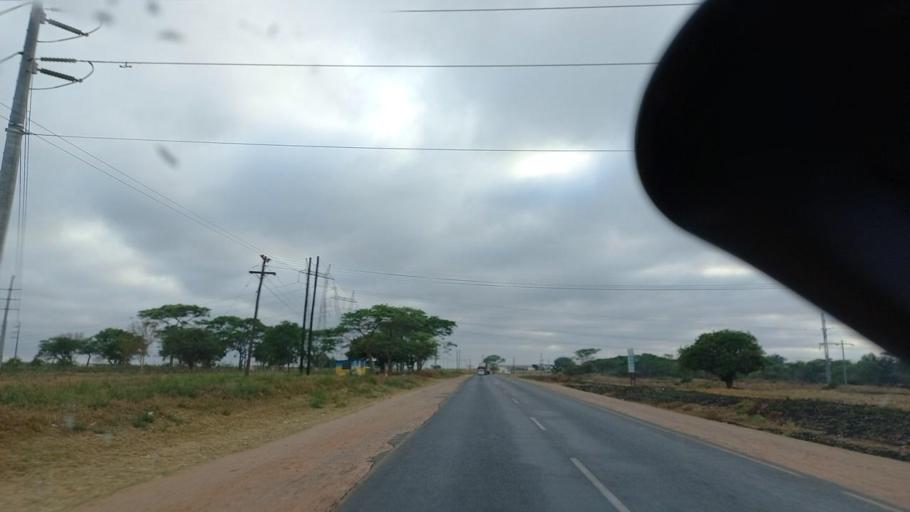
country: ZM
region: Lusaka
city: Chongwe
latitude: -15.3432
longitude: 28.5156
